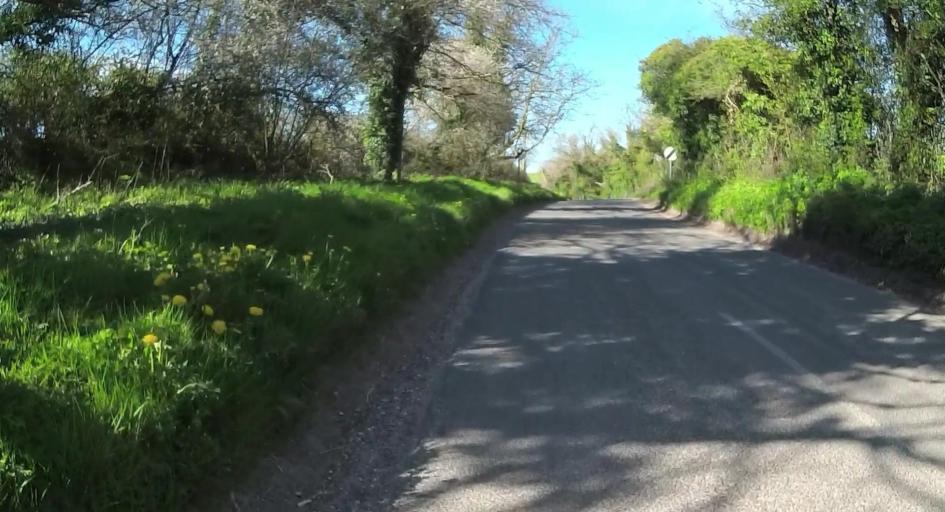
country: GB
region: England
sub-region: Hampshire
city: Abbotts Ann
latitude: 51.1381
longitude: -1.4859
